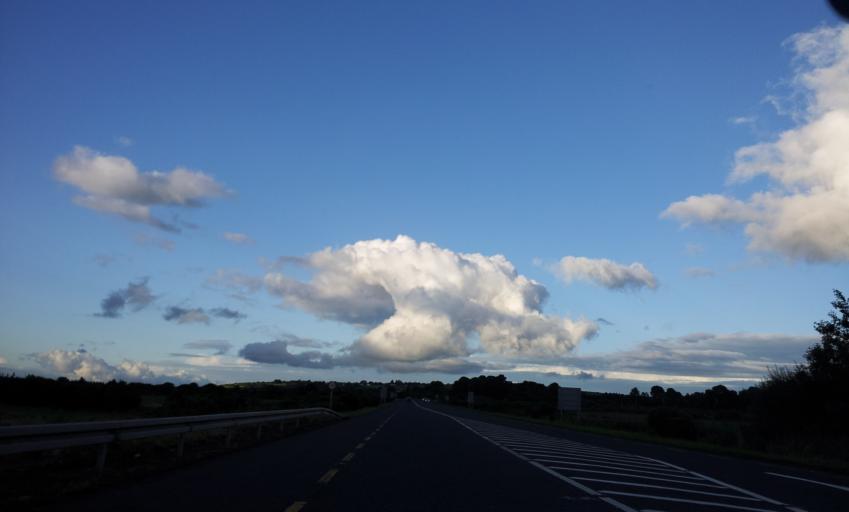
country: IE
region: Munster
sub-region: County Limerick
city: Abbeyfeale
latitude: 52.3450
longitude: -9.3407
